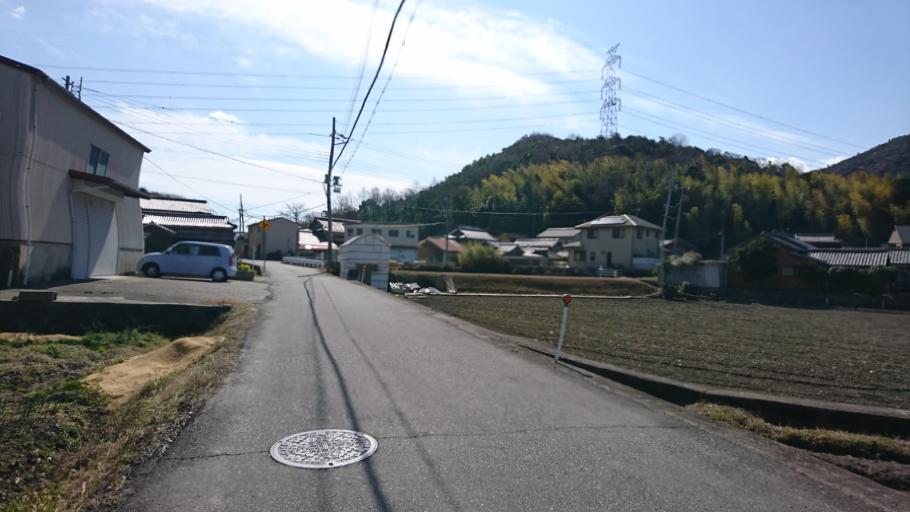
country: JP
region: Hyogo
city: Kakogawacho-honmachi
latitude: 34.8031
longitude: 134.8090
